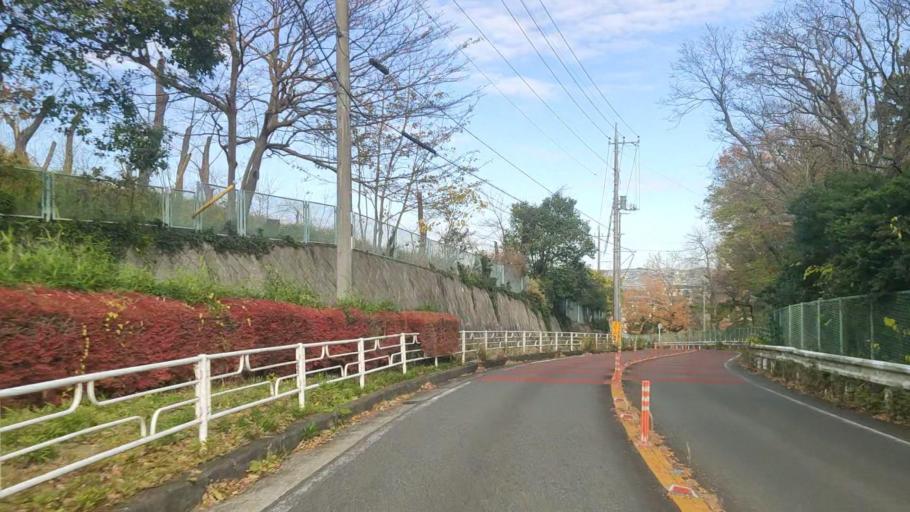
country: JP
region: Kanagawa
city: Minami-rinkan
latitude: 35.4517
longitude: 139.5391
